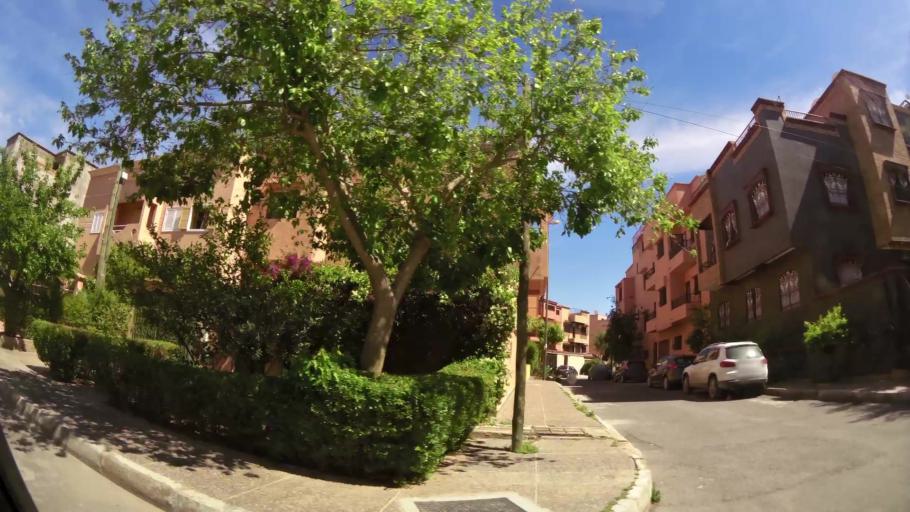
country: MA
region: Marrakech-Tensift-Al Haouz
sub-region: Marrakech
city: Marrakesh
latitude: 31.6749
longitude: -8.0009
